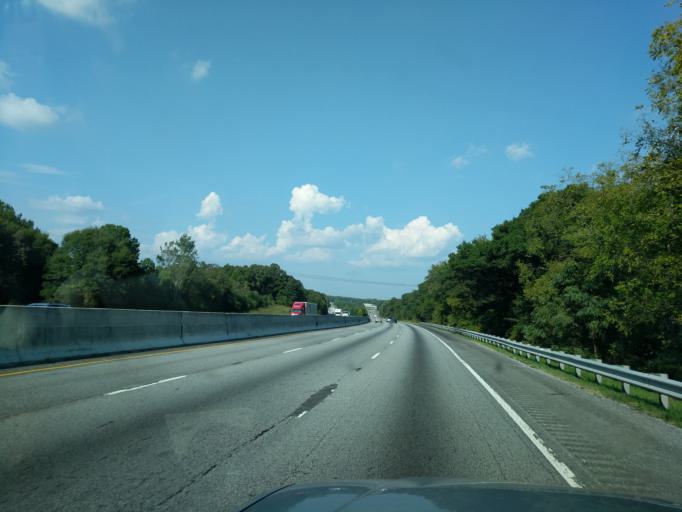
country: US
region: South Carolina
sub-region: Anderson County
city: Piedmont
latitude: 34.6841
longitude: -82.5167
